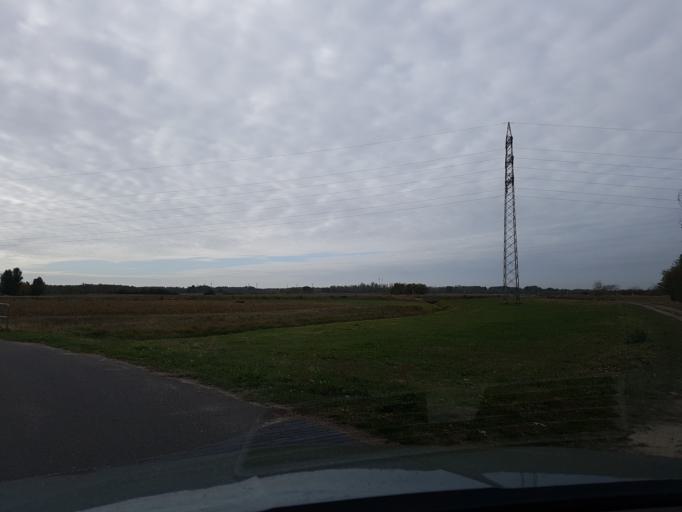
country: DE
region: Brandenburg
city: Falkenberg
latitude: 51.5651
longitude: 13.2482
